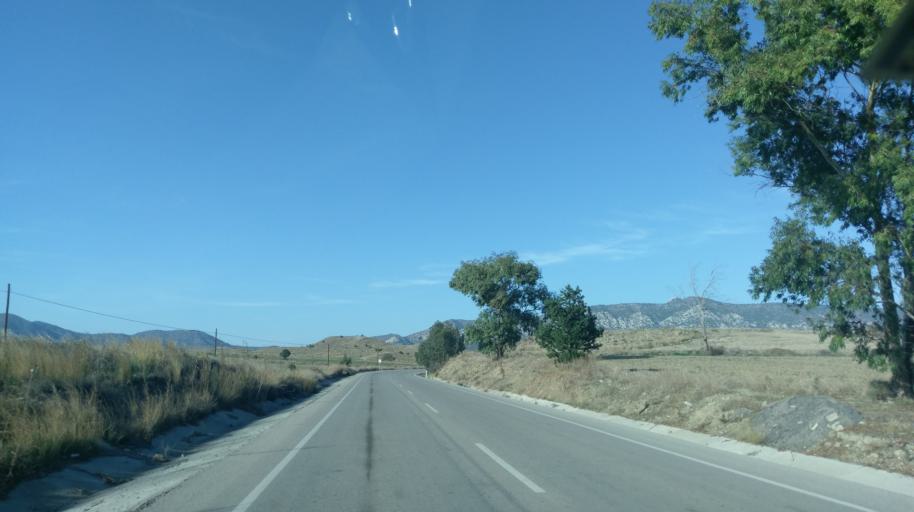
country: CY
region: Ammochostos
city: Lefkonoiko
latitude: 35.3019
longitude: 33.7335
